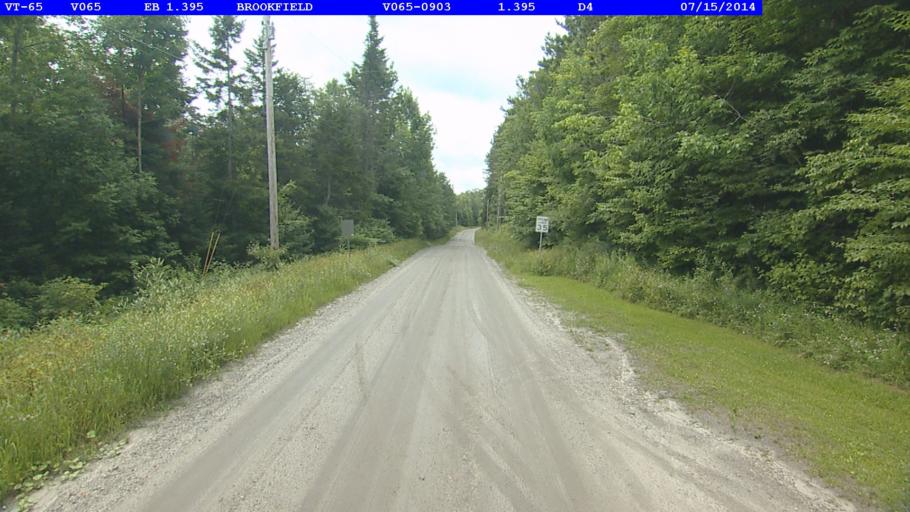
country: US
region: Vermont
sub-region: Washington County
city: Northfield
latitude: 44.0508
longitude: -72.6263
